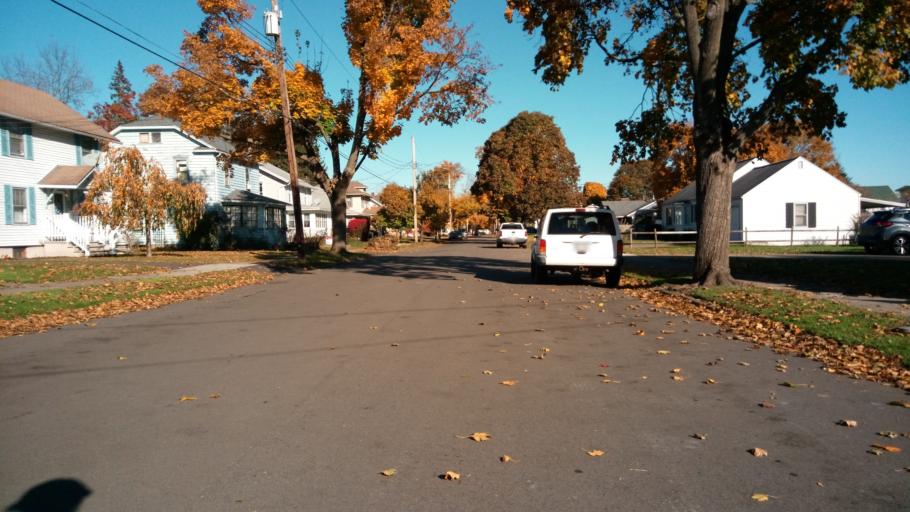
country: US
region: New York
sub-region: Chemung County
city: Southport
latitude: 42.0710
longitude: -76.8122
